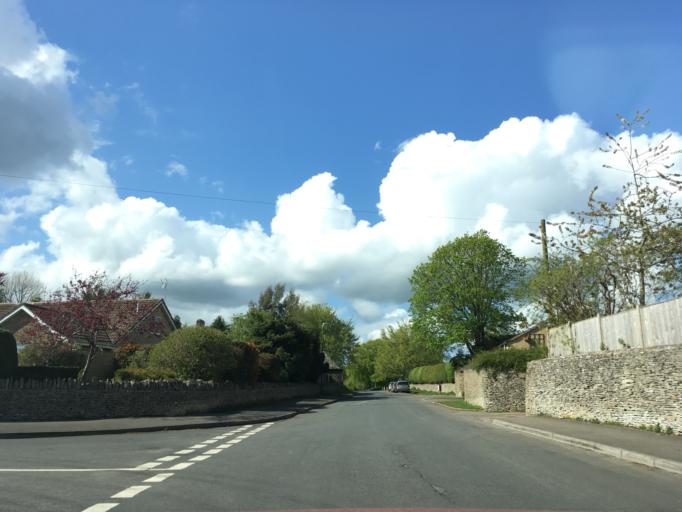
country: GB
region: England
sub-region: Gloucestershire
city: Minchinhampton
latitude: 51.7080
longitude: -2.1924
